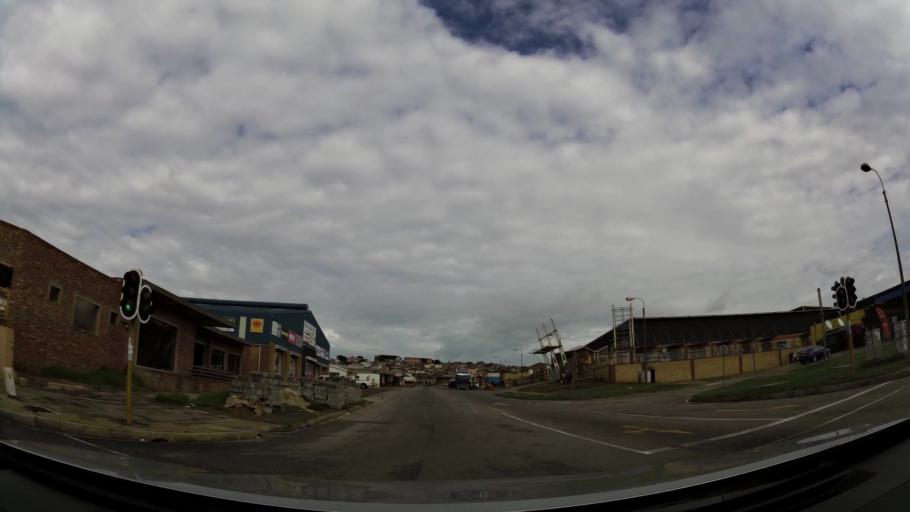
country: ZA
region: Eastern Cape
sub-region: Nelson Mandela Bay Metropolitan Municipality
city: Port Elizabeth
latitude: -33.9306
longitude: 25.5776
